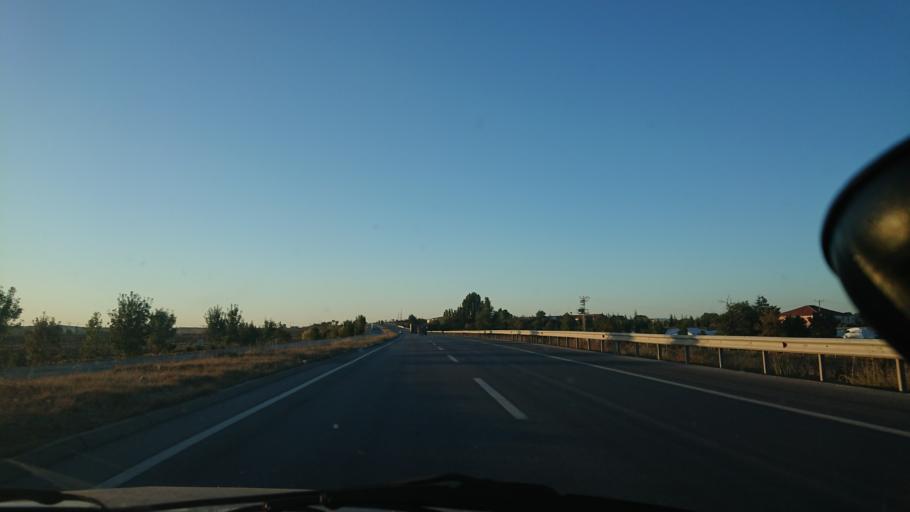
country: TR
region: Eskisehir
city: Mahmudiye
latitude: 39.4792
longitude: 30.9897
